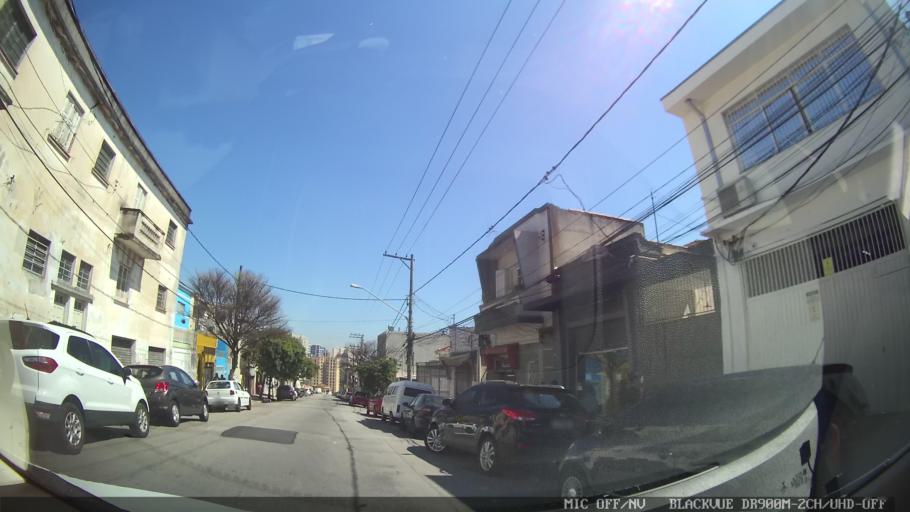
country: BR
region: Sao Paulo
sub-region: Sao Paulo
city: Sao Paulo
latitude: -23.5080
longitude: -46.6573
